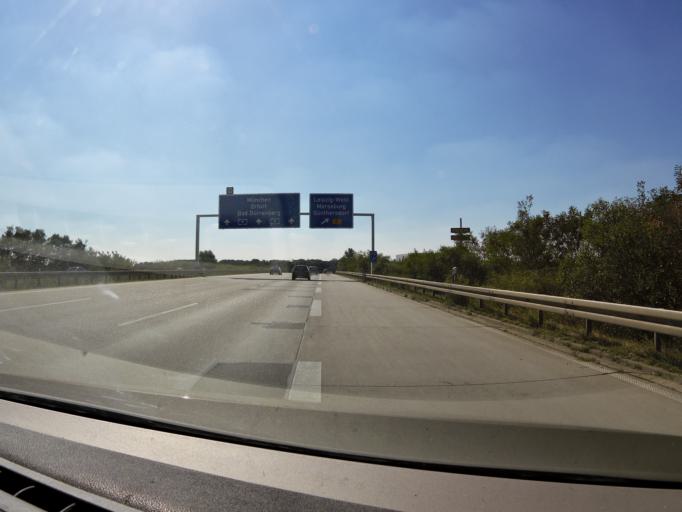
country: DE
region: Saxony-Anhalt
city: Gunthersdorf
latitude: 51.3531
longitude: 12.1875
